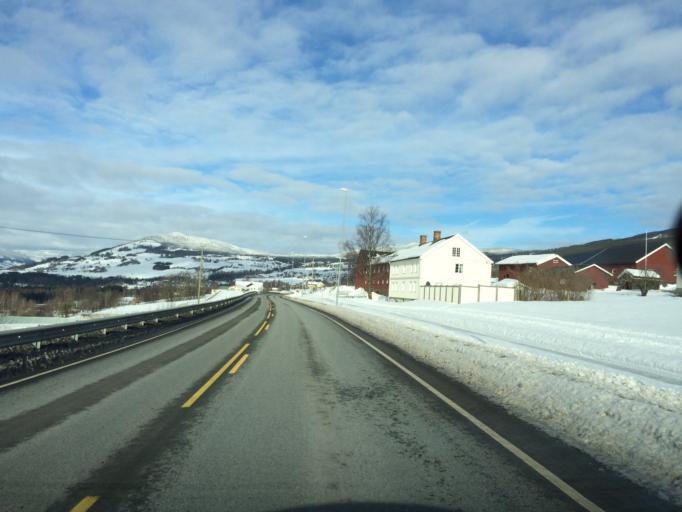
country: NO
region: Oppland
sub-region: Gausdal
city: Segalstad bru
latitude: 61.1985
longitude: 10.3081
